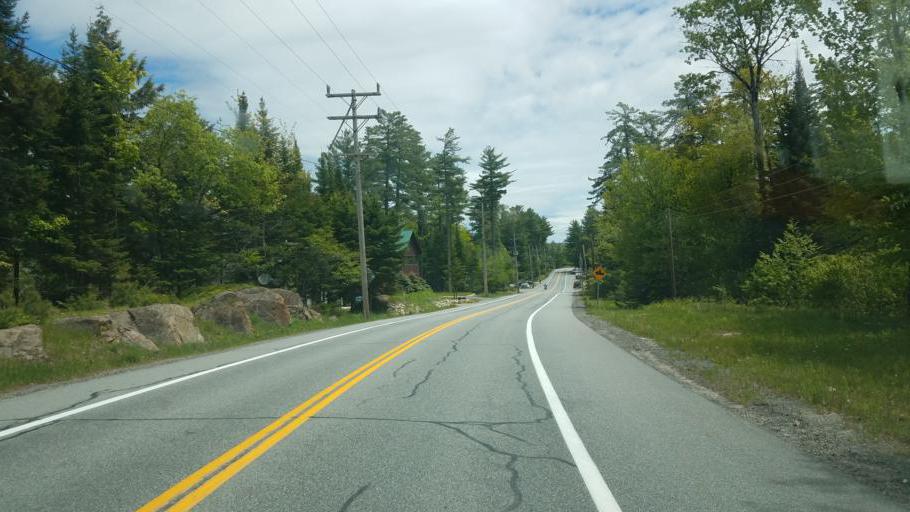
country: US
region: New York
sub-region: Hamilton County
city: Lake Pleasant
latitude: 43.8095
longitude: -74.6523
